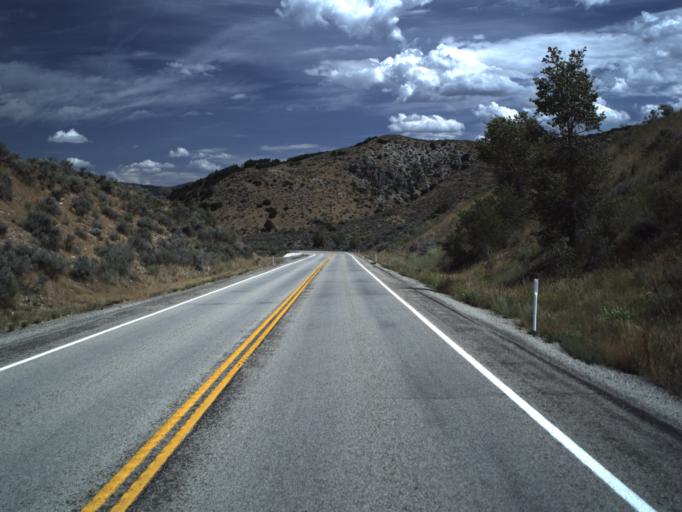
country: US
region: Utah
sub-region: Utah County
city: Woodland Hills
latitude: 39.9516
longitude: -111.5326
